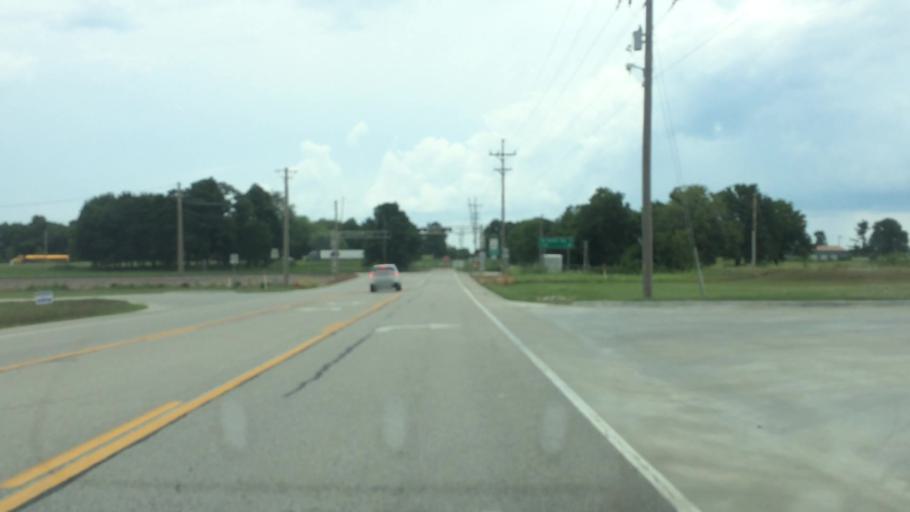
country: US
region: Missouri
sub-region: Greene County
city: Strafford
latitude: 37.2636
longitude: -93.1356
